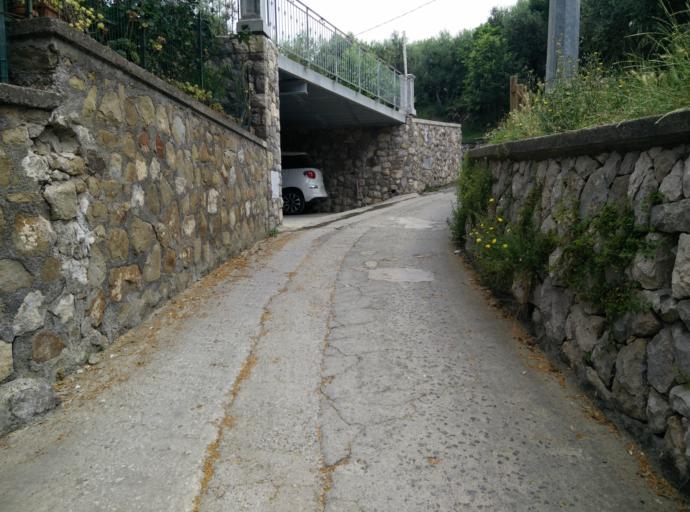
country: IT
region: Campania
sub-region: Provincia di Napoli
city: Massa Lubrense
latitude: 40.5993
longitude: 14.3828
